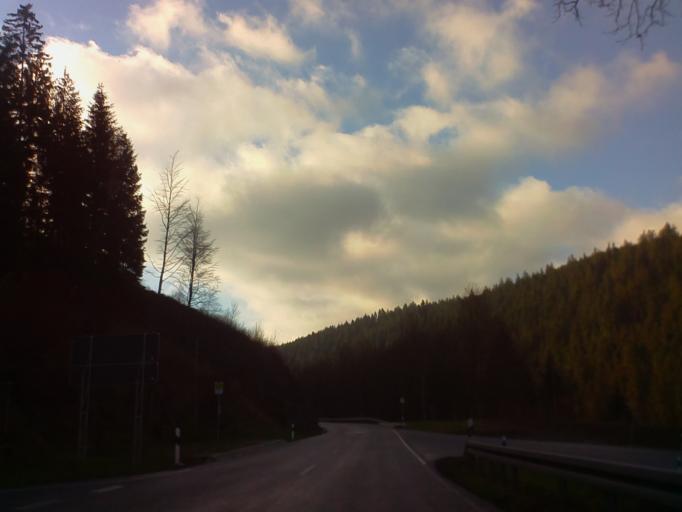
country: DE
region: Thuringia
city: Meuselbach
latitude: 50.5735
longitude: 11.0741
